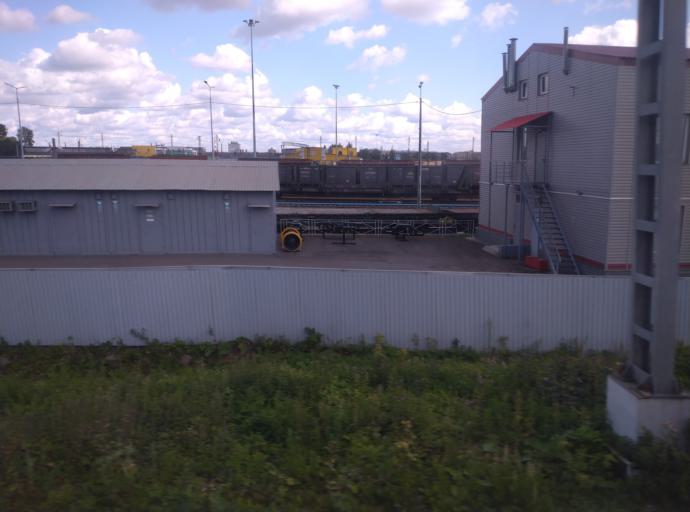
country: RU
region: St.-Petersburg
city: Obukhovo
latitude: 59.8694
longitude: 30.4209
